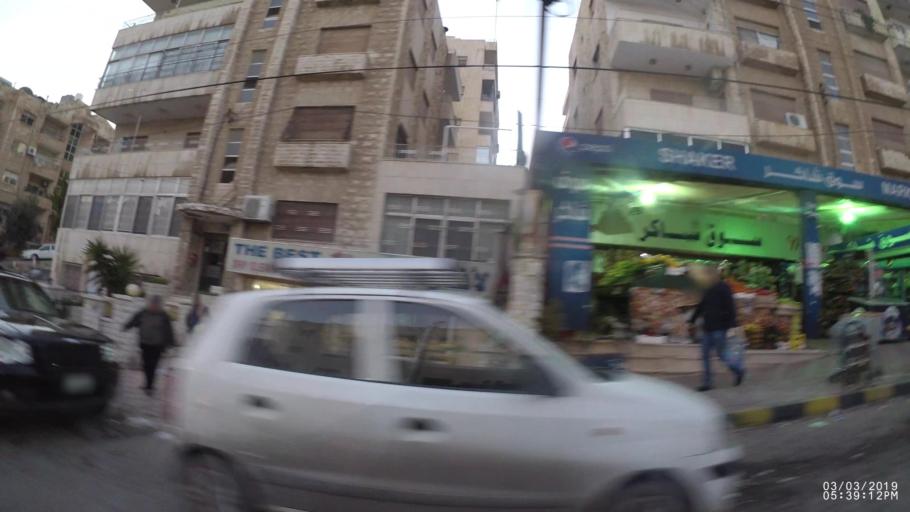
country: JO
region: Amman
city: Al Jubayhah
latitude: 31.9897
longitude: 35.8852
